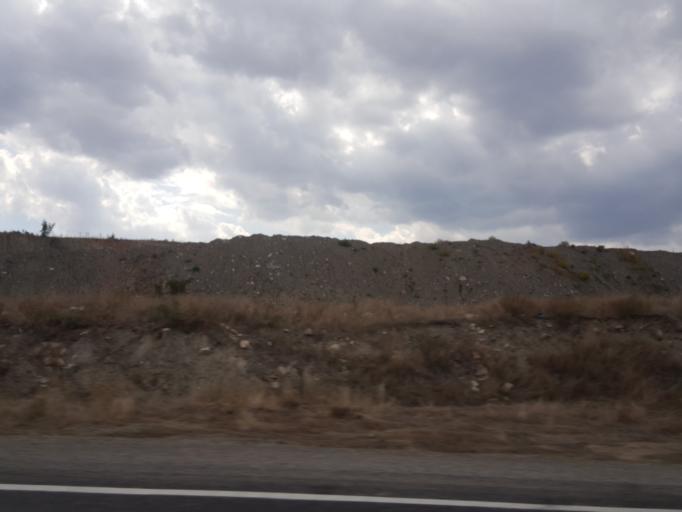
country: TR
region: Yozgat
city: Cekerek
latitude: 40.1893
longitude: 35.4409
